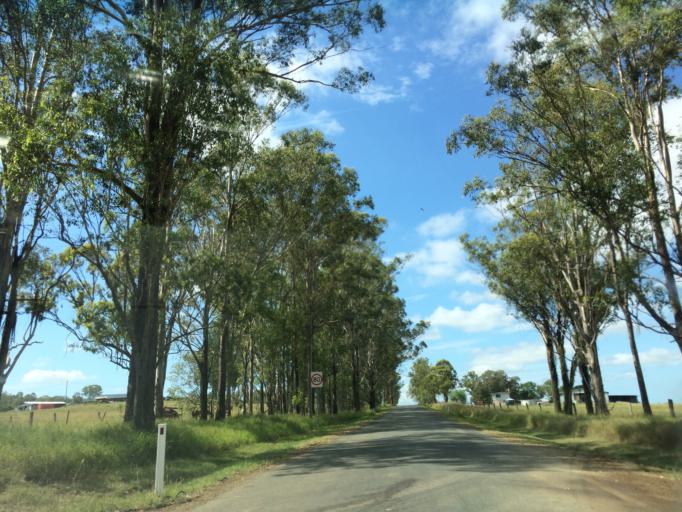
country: AU
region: Queensland
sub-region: Logan
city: Cedar Vale
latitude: -27.8836
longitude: 152.9720
